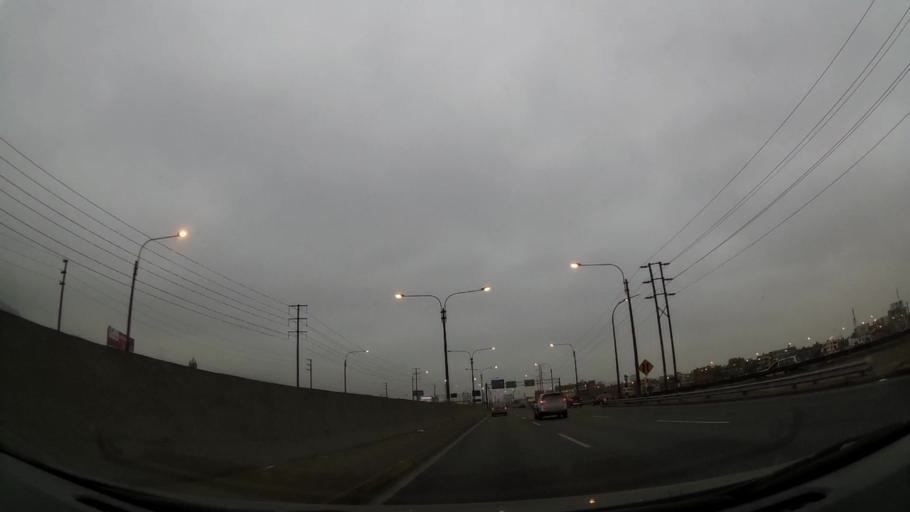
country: PE
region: Lima
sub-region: Lima
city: Independencia
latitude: -11.9615
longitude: -77.0686
